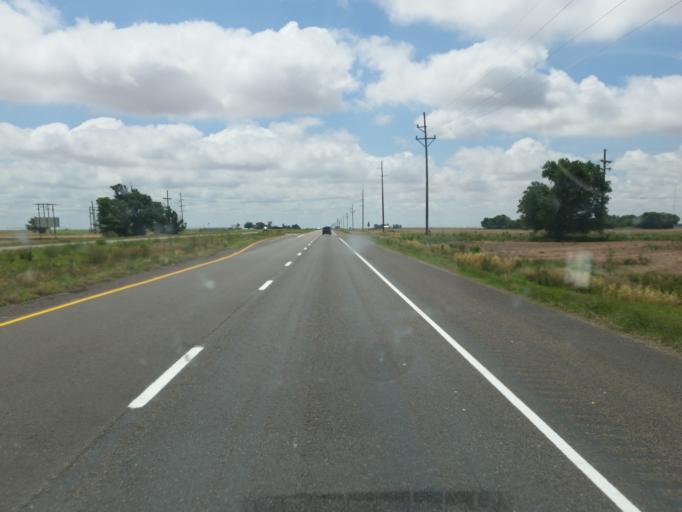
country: US
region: Texas
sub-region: Lubbock County
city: Slaton
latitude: 33.4048
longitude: -101.6194
